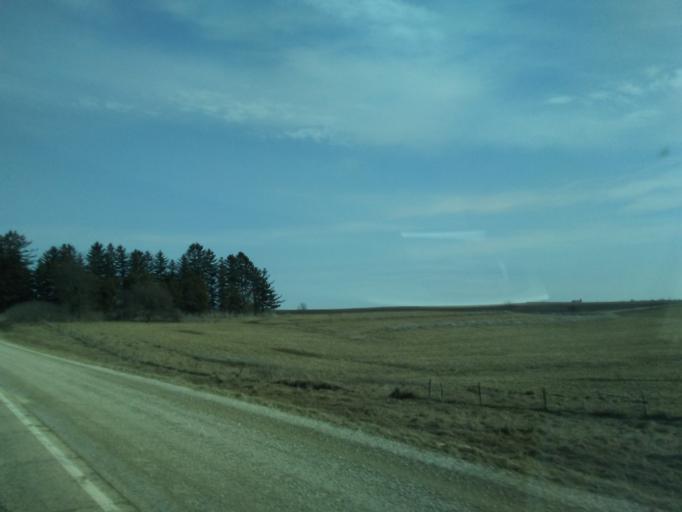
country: US
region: Iowa
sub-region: Allamakee County
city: Waukon
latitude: 43.2041
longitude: -91.4130
